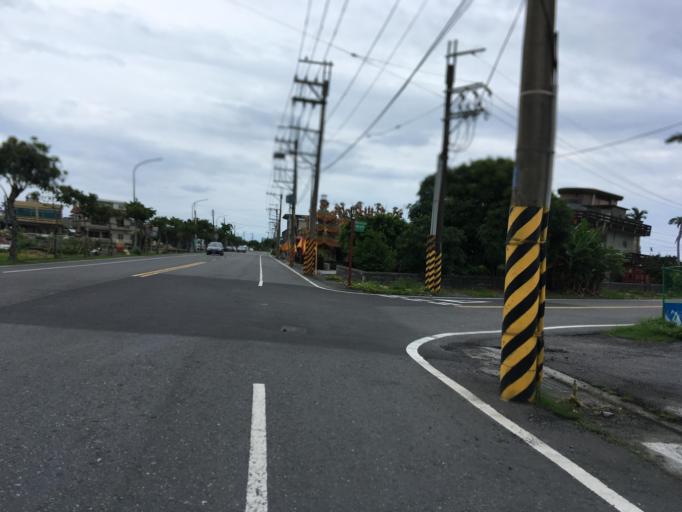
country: TW
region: Taiwan
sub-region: Yilan
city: Yilan
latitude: 24.6880
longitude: 121.8034
